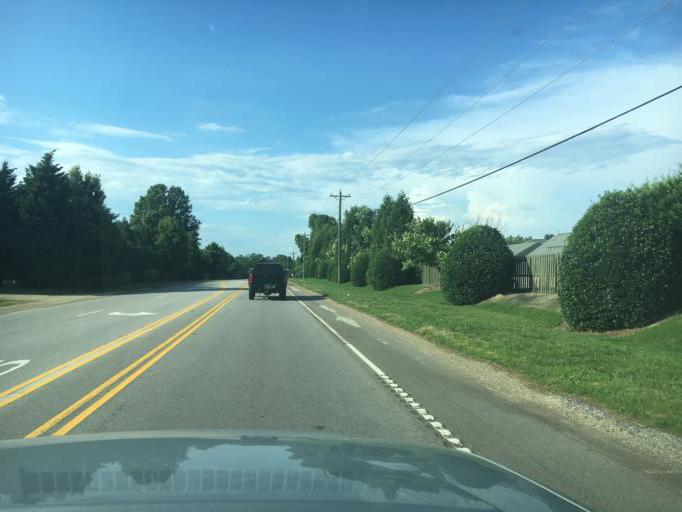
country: US
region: South Carolina
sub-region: Greenville County
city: Simpsonville
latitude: 34.7695
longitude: -82.2580
